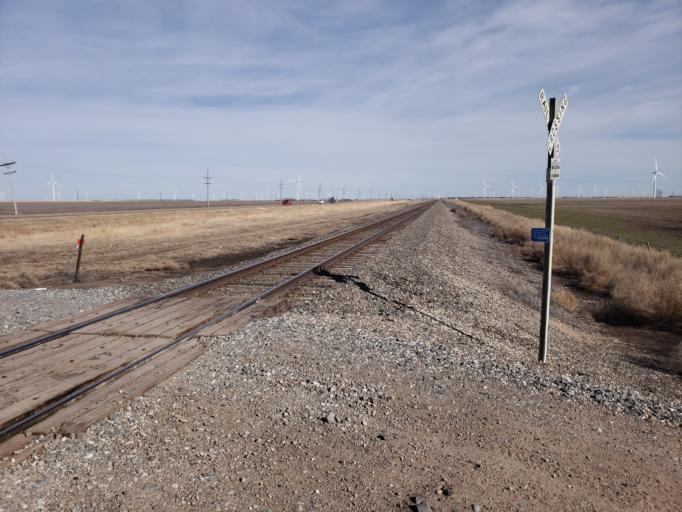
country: US
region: Kansas
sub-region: Ford County
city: Dodge City
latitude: 37.8125
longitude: -99.8328
